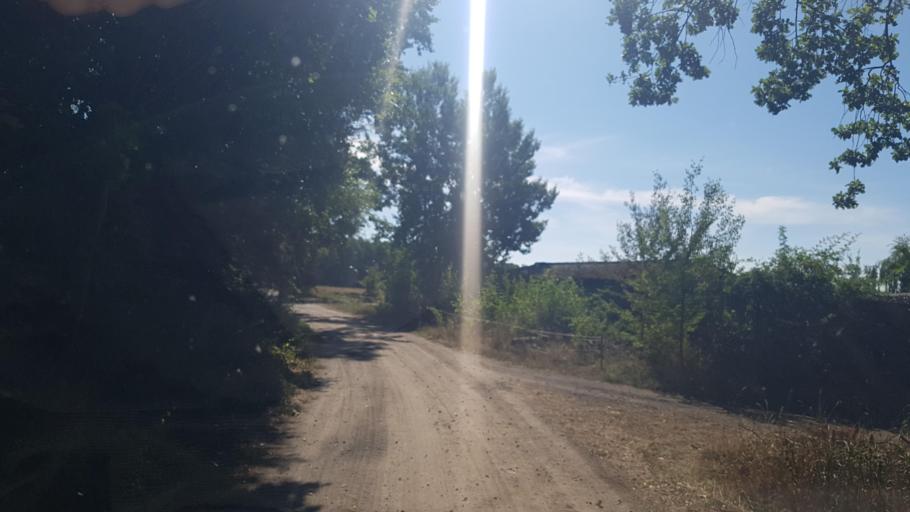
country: DE
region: Brandenburg
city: Brandenburg an der Havel
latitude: 52.3423
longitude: 12.5324
